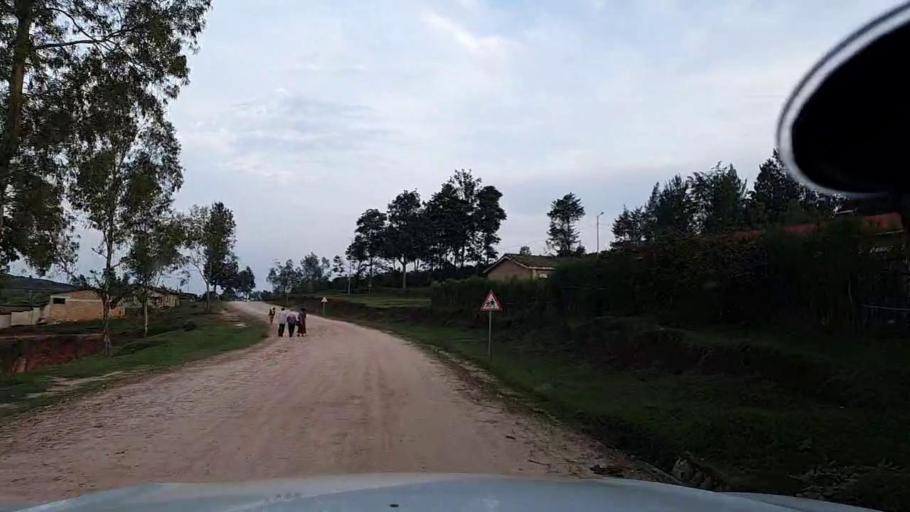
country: RW
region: Southern Province
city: Nyanza
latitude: -2.2232
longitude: 29.6502
